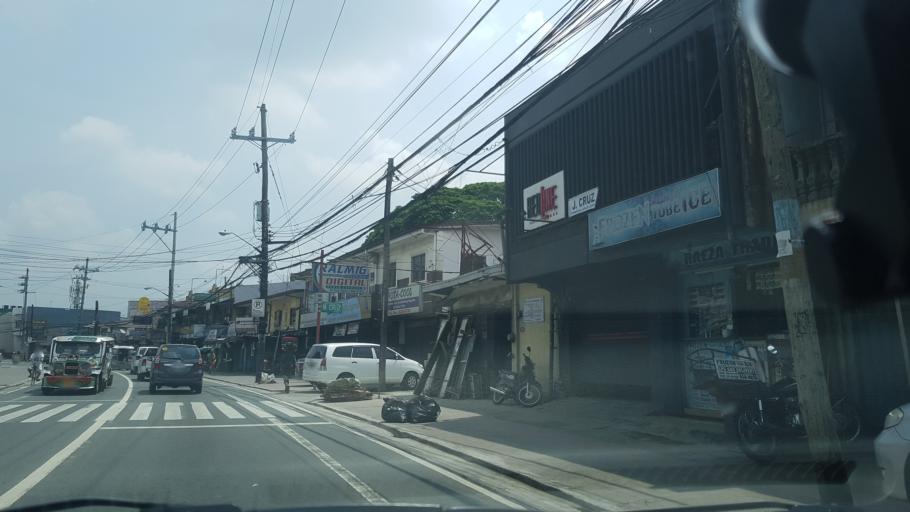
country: PH
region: Metro Manila
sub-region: Marikina
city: Calumpang
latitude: 14.6493
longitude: 121.1010
